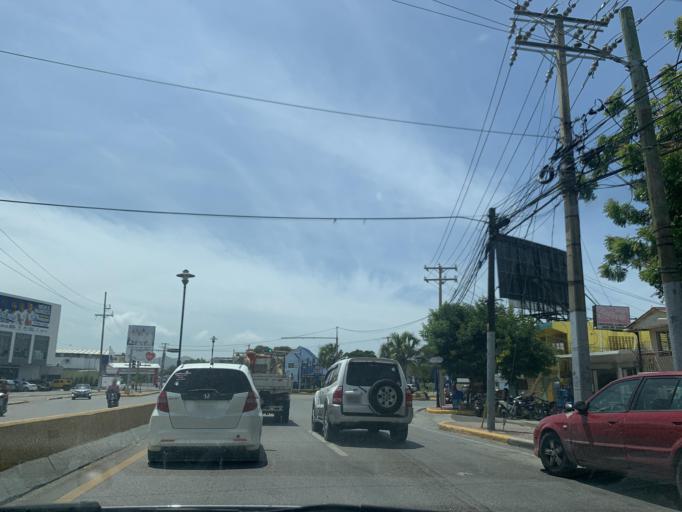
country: DO
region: Puerto Plata
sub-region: Puerto Plata
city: Puerto Plata
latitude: 19.7903
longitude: -70.7004
